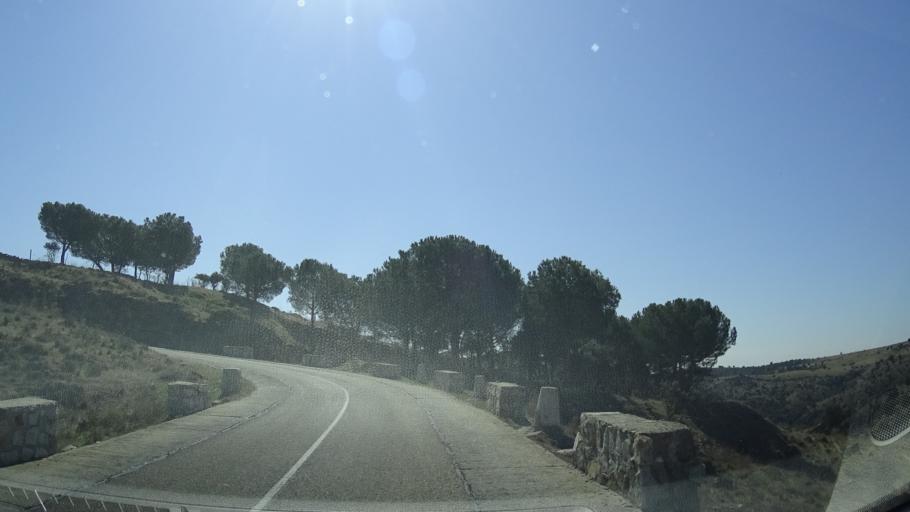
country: ES
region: Madrid
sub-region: Provincia de Madrid
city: Colmenar Viejo
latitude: 40.6473
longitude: -3.8069
